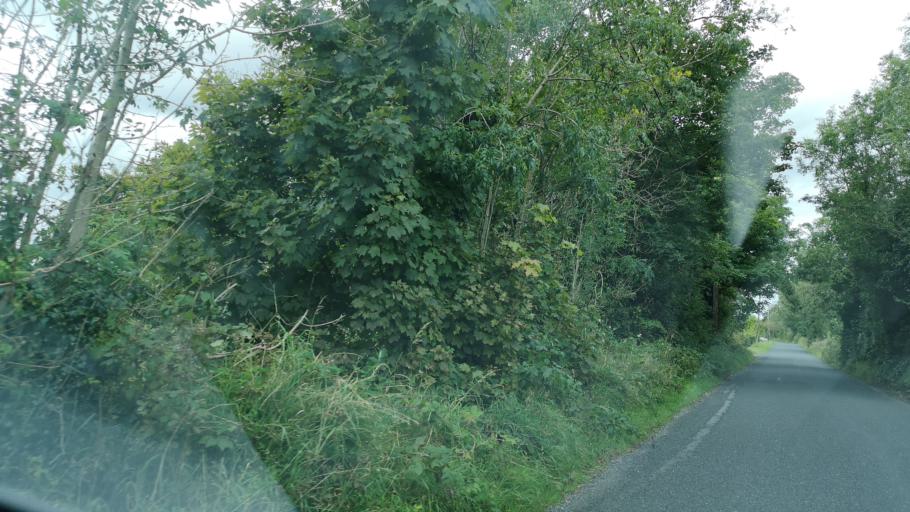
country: IE
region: Connaught
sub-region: County Galway
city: Loughrea
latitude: 53.1608
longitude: -8.4611
